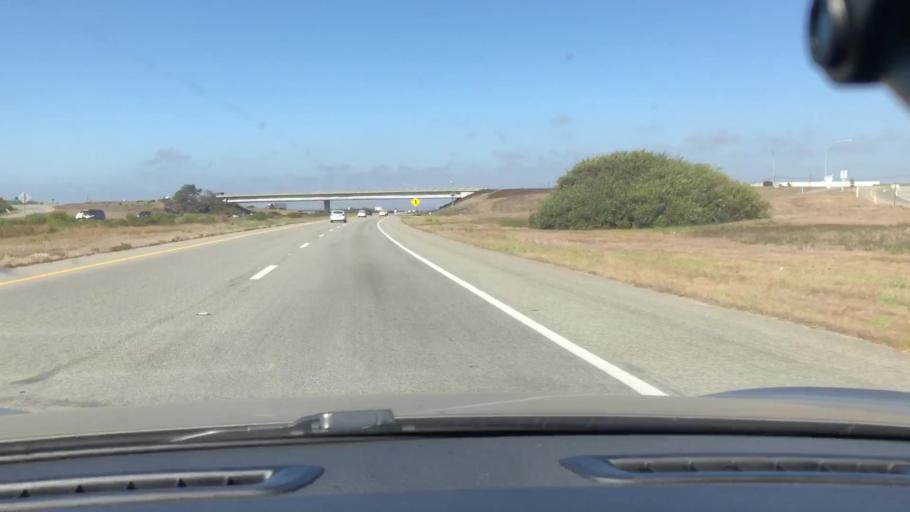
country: US
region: California
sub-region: Monterey County
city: Marina
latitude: 36.7227
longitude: -121.7908
